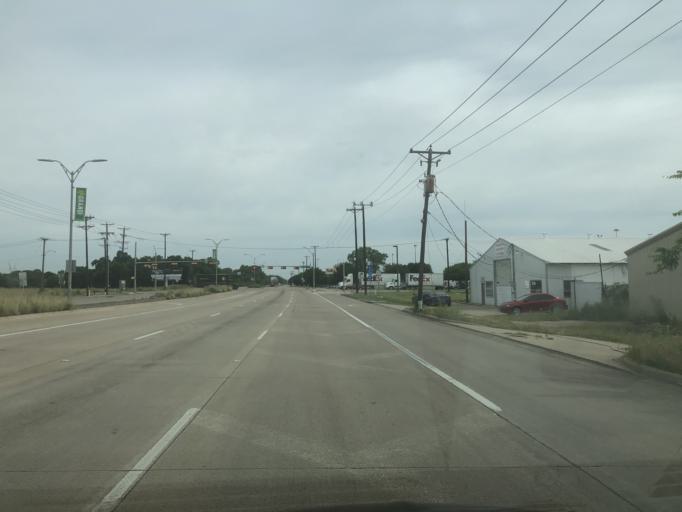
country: US
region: Texas
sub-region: Dallas County
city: Grand Prairie
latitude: 32.7766
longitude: -96.9945
